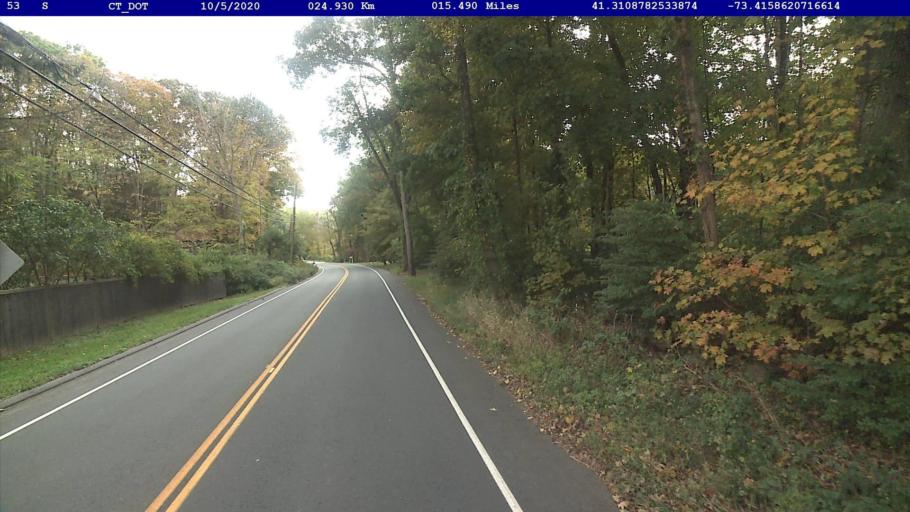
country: US
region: Connecticut
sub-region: Fairfield County
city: Georgetown
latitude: 41.3109
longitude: -73.4158
